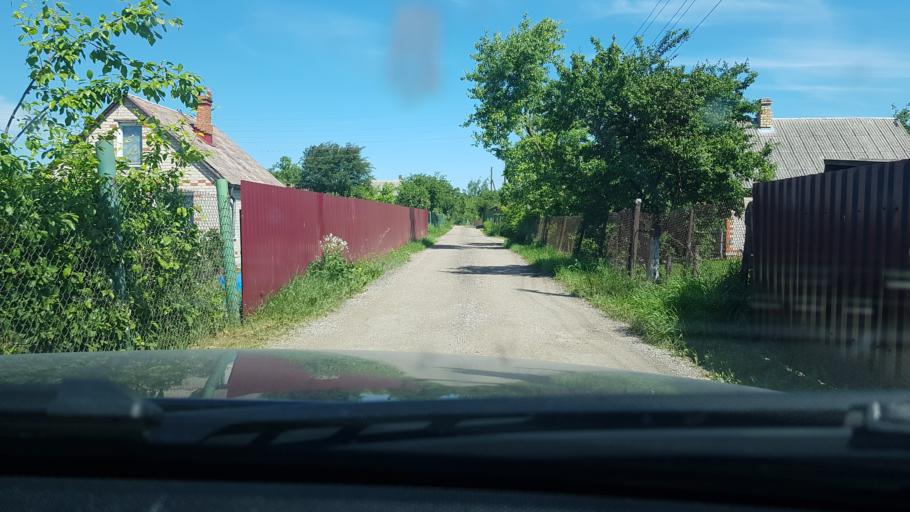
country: LV
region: Daugavpils
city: Daugavpils
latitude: 55.8586
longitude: 26.5749
